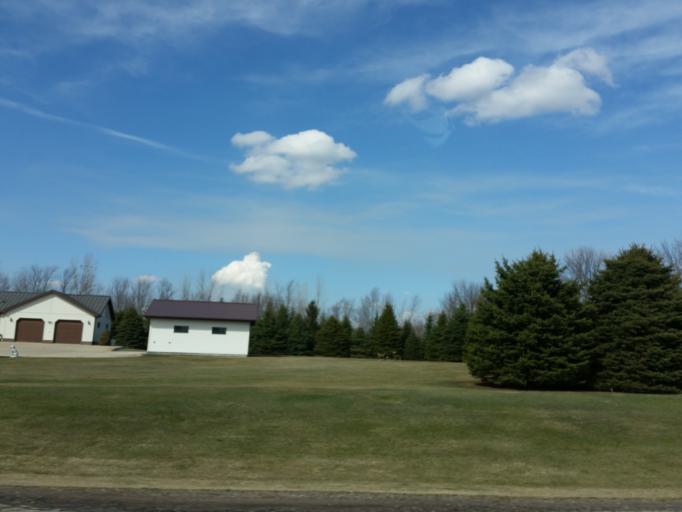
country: US
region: Minnesota
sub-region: Lac qui Parle County
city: Madison
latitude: 44.9356
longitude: -96.3918
